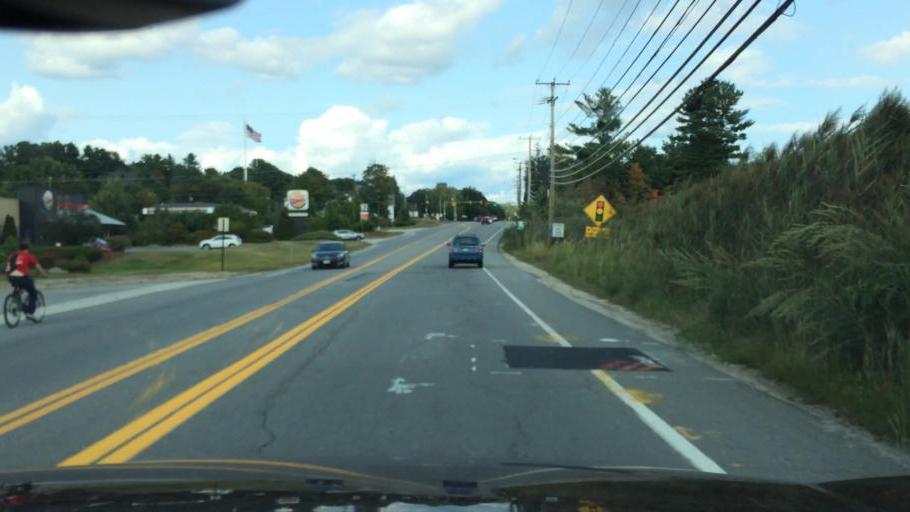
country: US
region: New Hampshire
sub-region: Hillsborough County
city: Hudson
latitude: 42.7698
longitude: -71.4109
